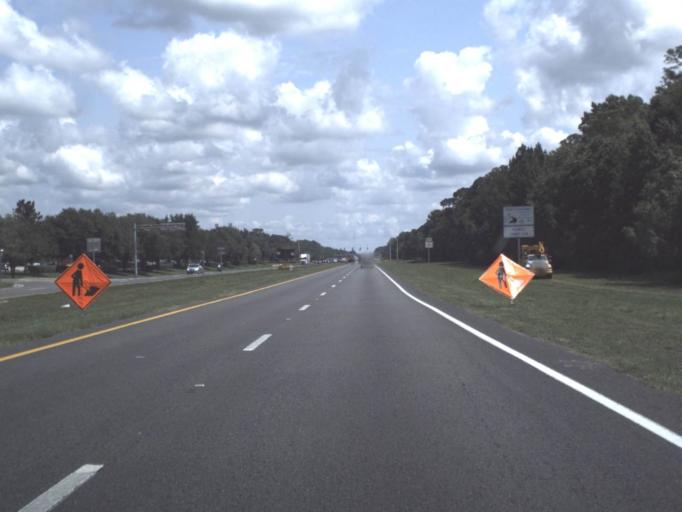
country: US
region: Florida
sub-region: Saint Johns County
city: Fruit Cove
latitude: 30.1807
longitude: -81.5515
